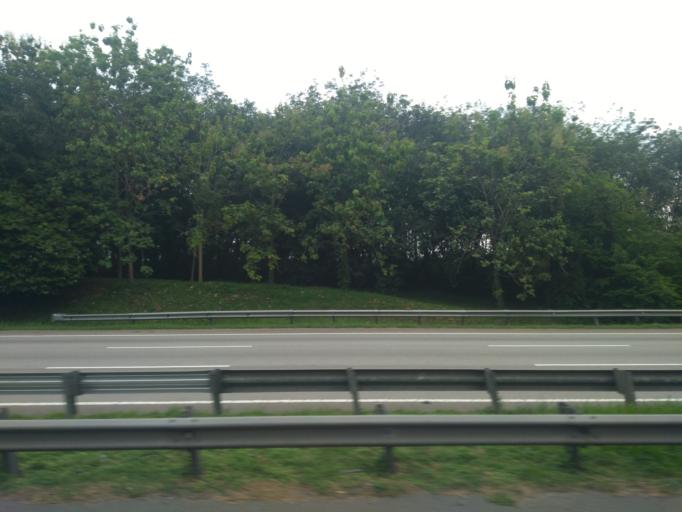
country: MY
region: Melaka
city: Alor Gajah
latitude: 2.3784
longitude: 102.2340
